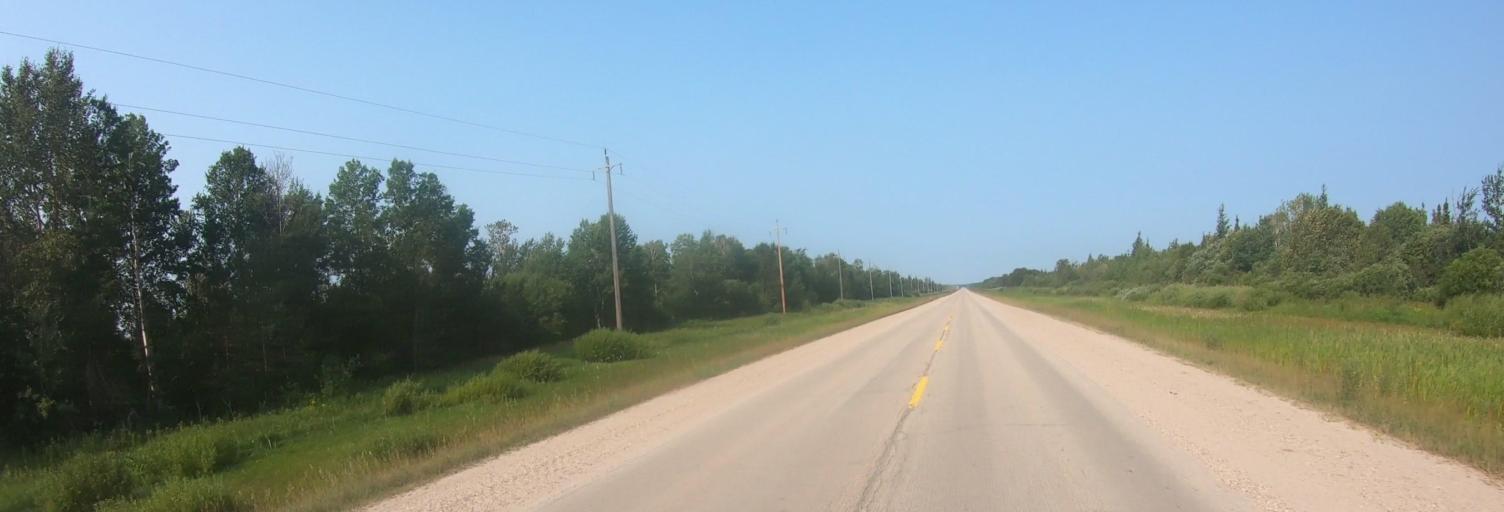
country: US
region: Minnesota
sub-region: Roseau County
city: Roseau
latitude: 49.0235
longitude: -95.6643
